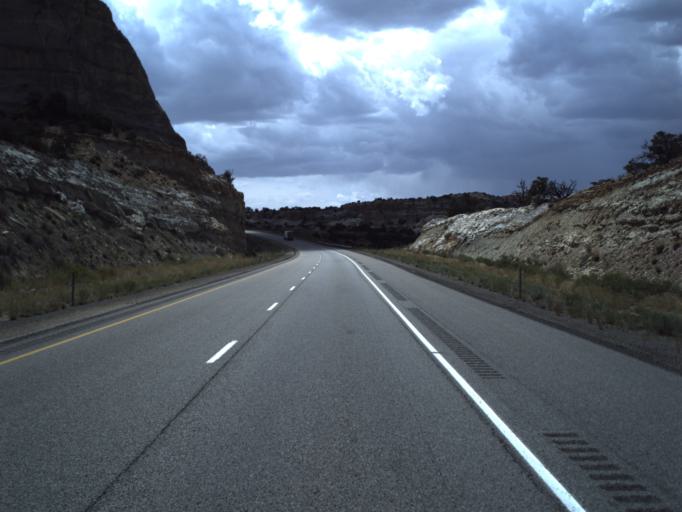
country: US
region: Utah
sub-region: Emery County
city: Ferron
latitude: 38.8549
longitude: -110.8758
